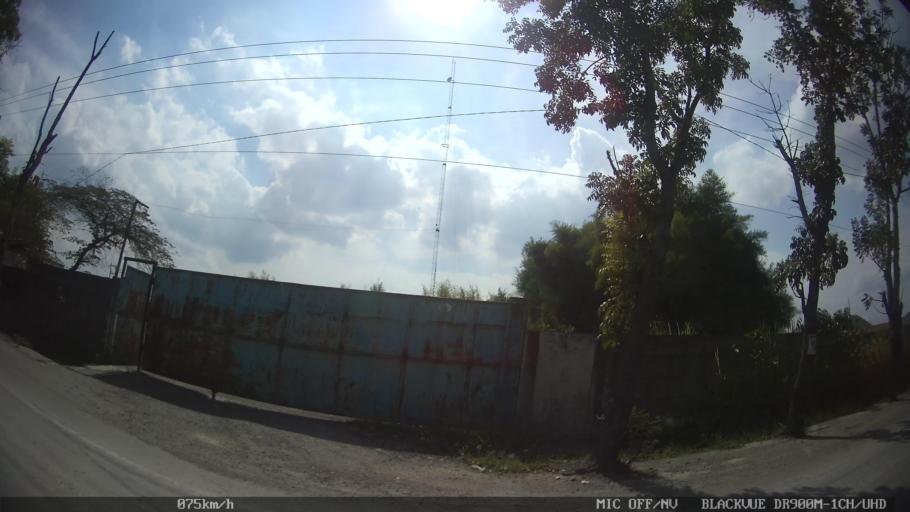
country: ID
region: North Sumatra
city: Binjai
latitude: 3.6314
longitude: 98.5350
